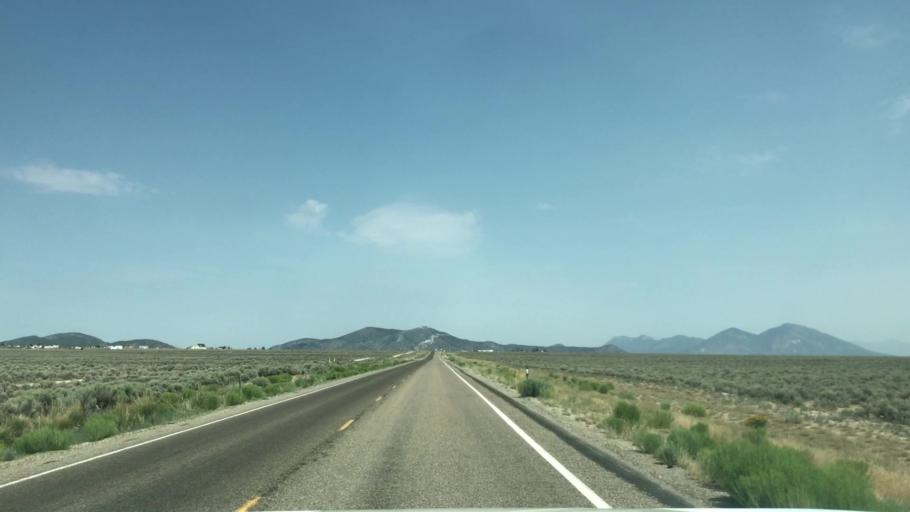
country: US
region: Nevada
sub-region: White Pine County
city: Ely
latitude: 39.1887
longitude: -114.8339
